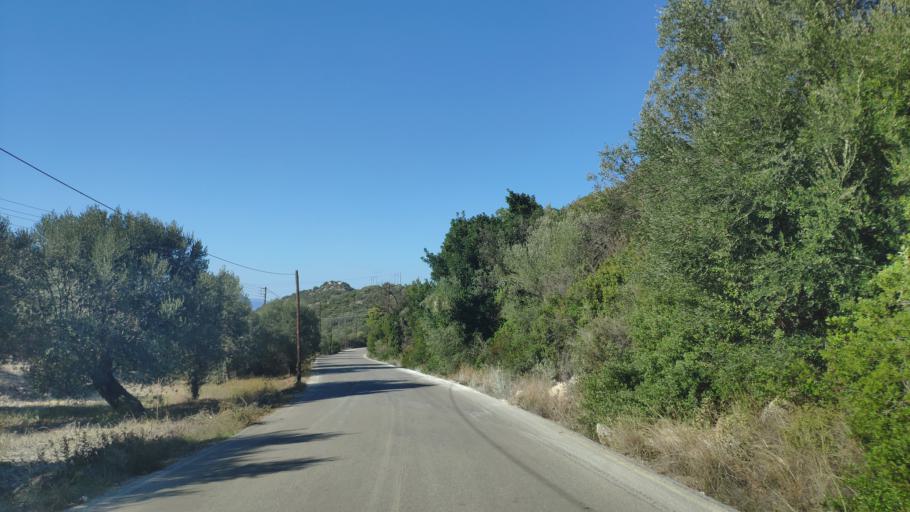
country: GR
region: Attica
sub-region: Nomos Piraios
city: Galatas
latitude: 37.5495
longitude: 23.3735
